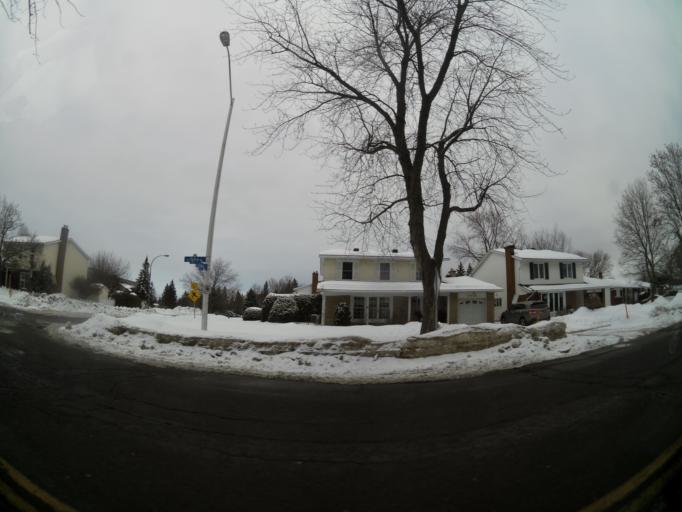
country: CA
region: Quebec
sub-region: Outaouais
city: Gatineau
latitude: 45.4577
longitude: -75.6009
